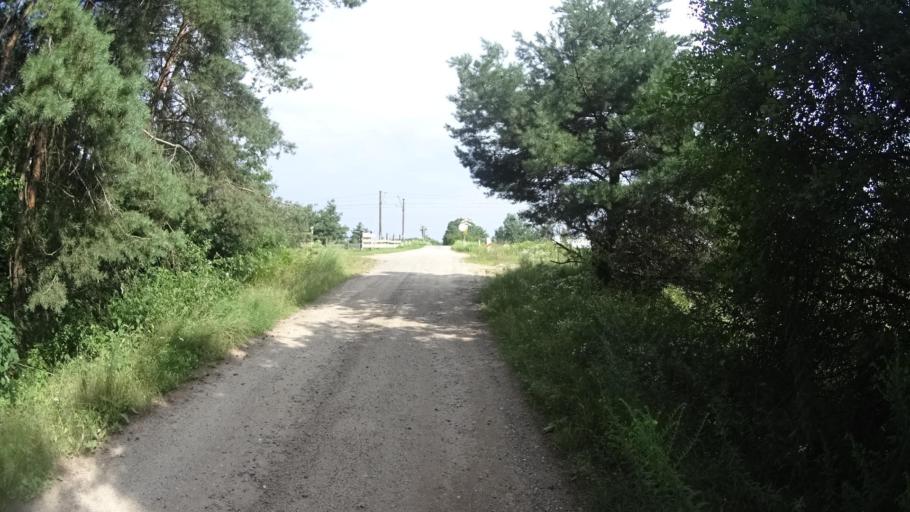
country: PL
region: Masovian Voivodeship
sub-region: Powiat piaseczynski
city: Tarczyn
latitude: 51.9704
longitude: 20.8542
